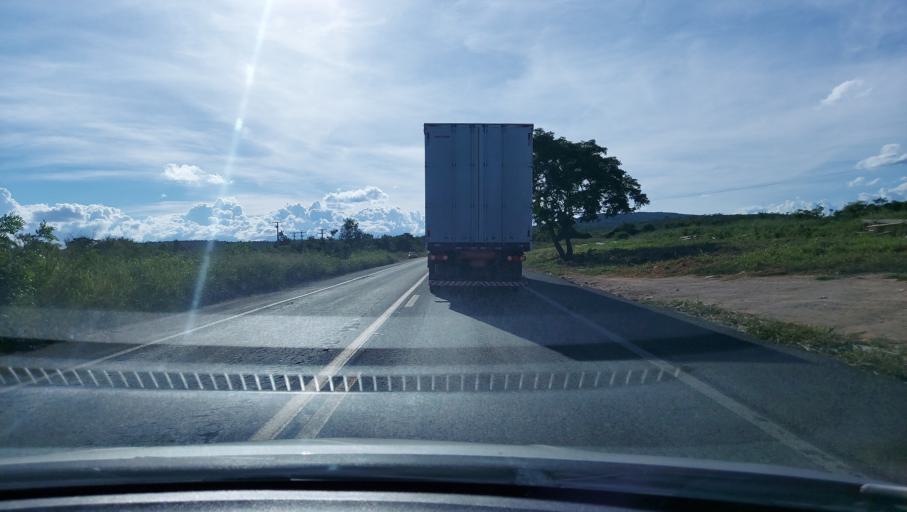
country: BR
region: Bahia
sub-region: Seabra
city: Seabra
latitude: -12.4300
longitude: -41.7897
